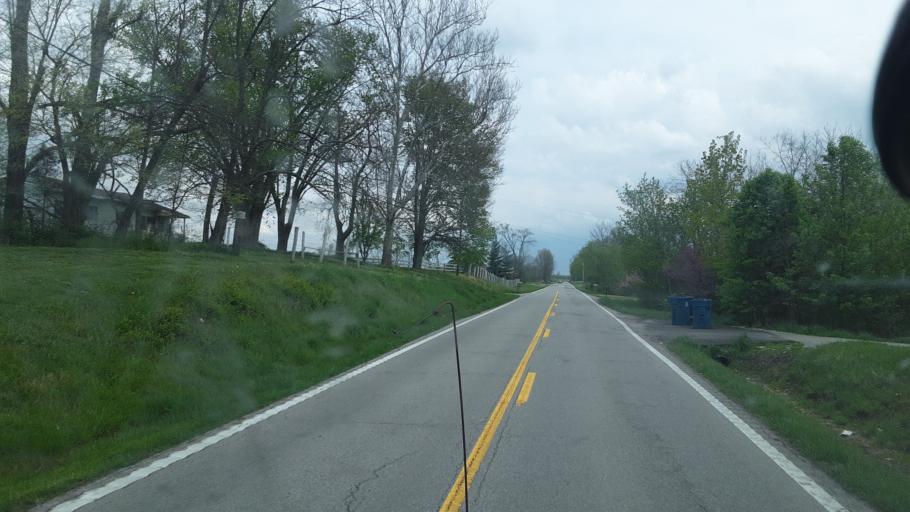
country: US
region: Kentucky
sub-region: Grant County
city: Dry Ridge
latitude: 38.6623
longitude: -84.6629
